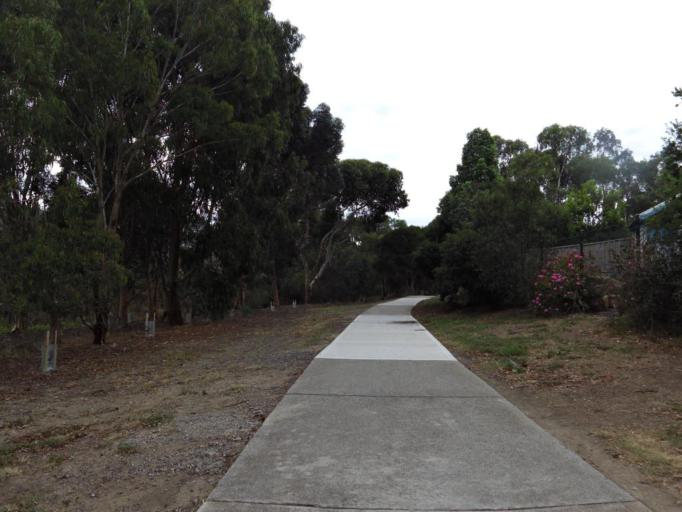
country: AU
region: Victoria
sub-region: Hume
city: Attwood
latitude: -37.6712
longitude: 144.8959
